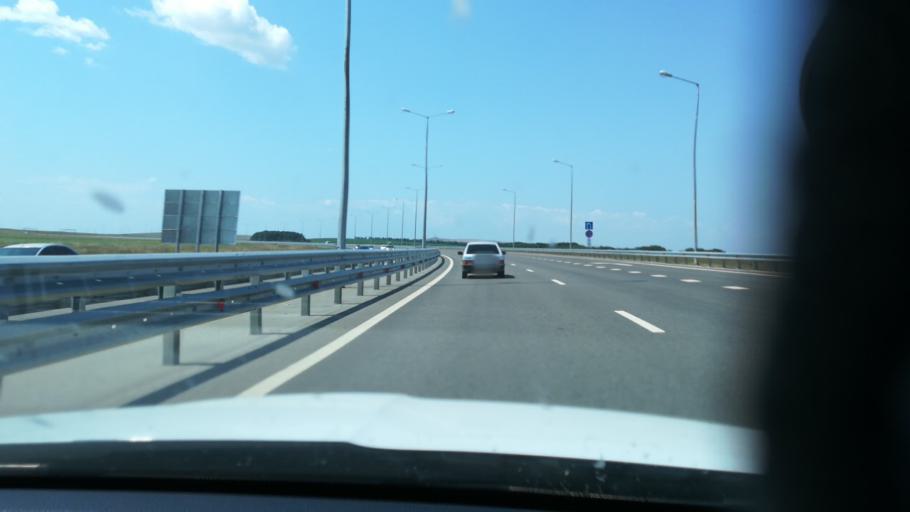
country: RU
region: Krasnodarskiy
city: Vyshestebliyevskaya
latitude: 45.2448
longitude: 37.0603
